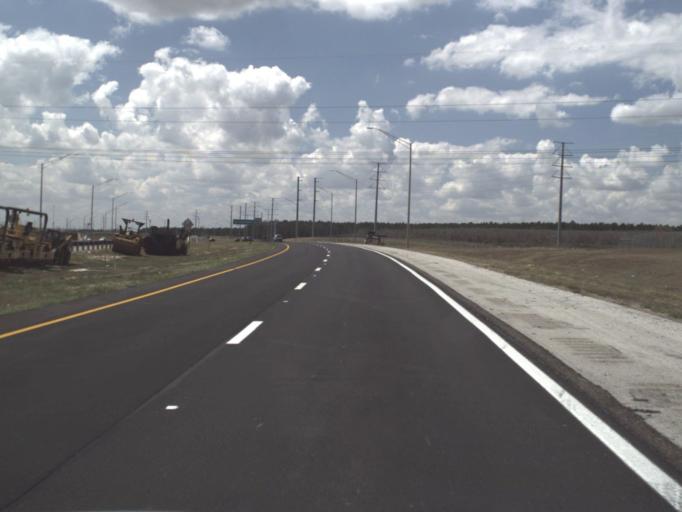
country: US
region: Florida
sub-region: Orange County
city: Oakland
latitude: 28.4825
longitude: -81.6306
